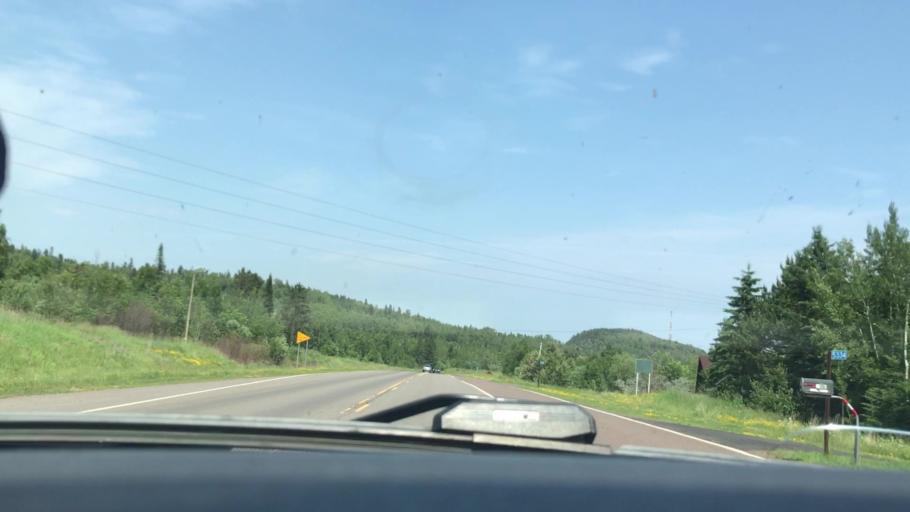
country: US
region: Minnesota
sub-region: Lake County
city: Silver Bay
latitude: 47.3108
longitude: -91.2358
